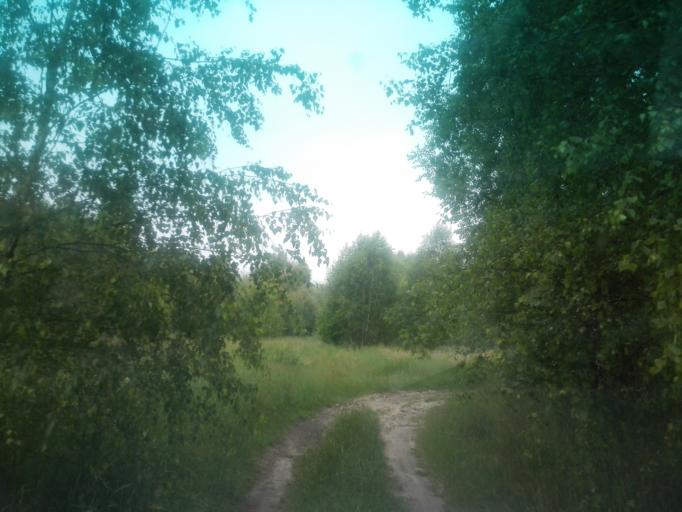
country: PL
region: Silesian Voivodeship
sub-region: Powiat czestochowski
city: Olsztyn
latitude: 50.7871
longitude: 19.2710
